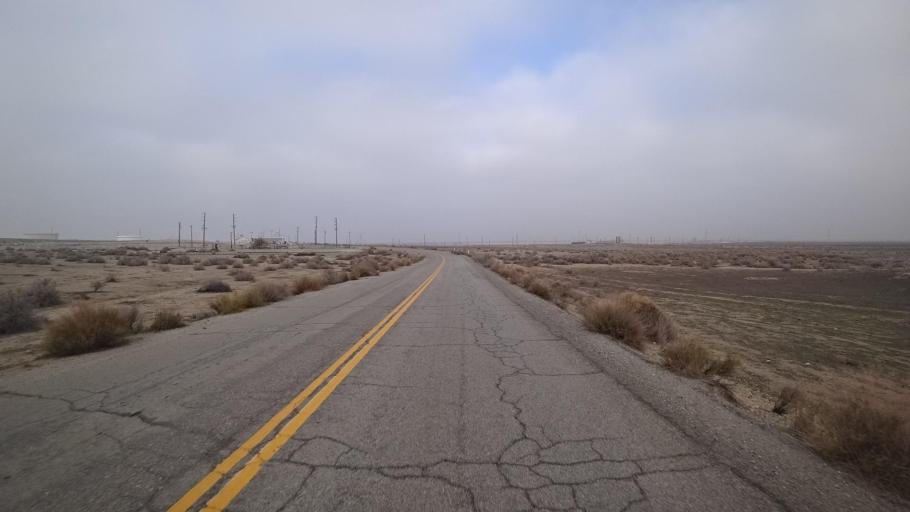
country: US
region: California
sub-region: Kern County
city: Maricopa
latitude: 35.1501
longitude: -119.3370
